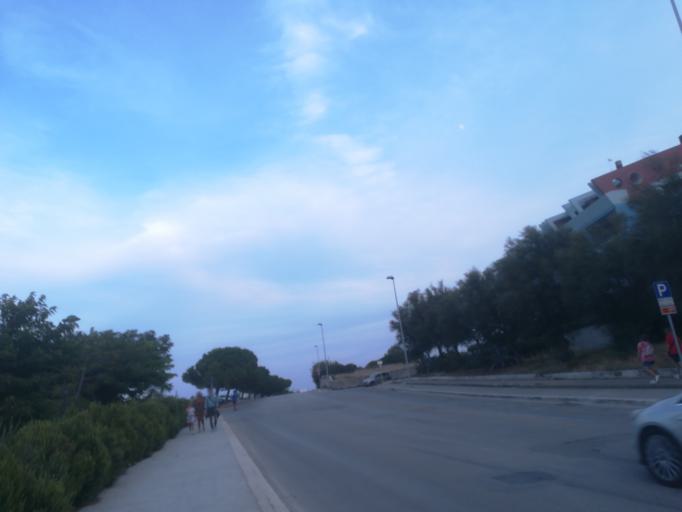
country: IT
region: Apulia
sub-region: Provincia di Bari
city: Monopoli
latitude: 40.9453
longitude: 17.3093
